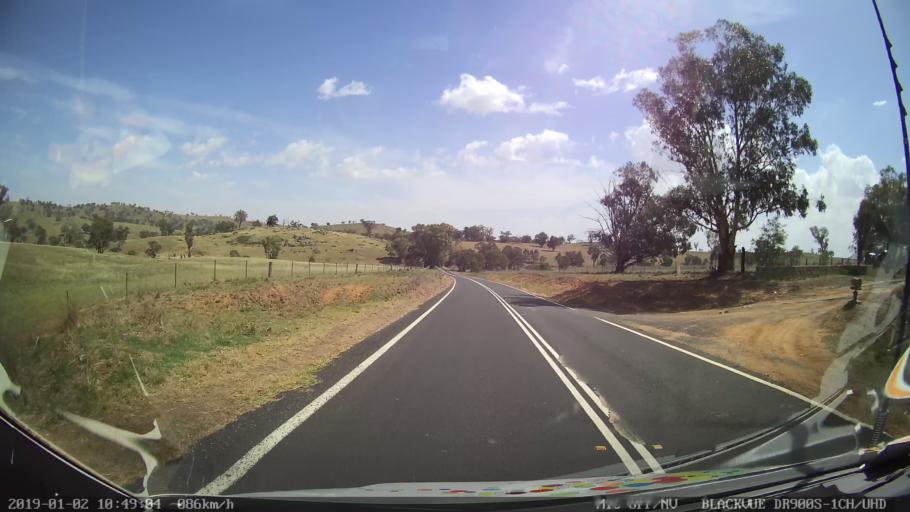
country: AU
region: New South Wales
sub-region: Cootamundra
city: Cootamundra
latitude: -34.7292
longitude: 148.2777
